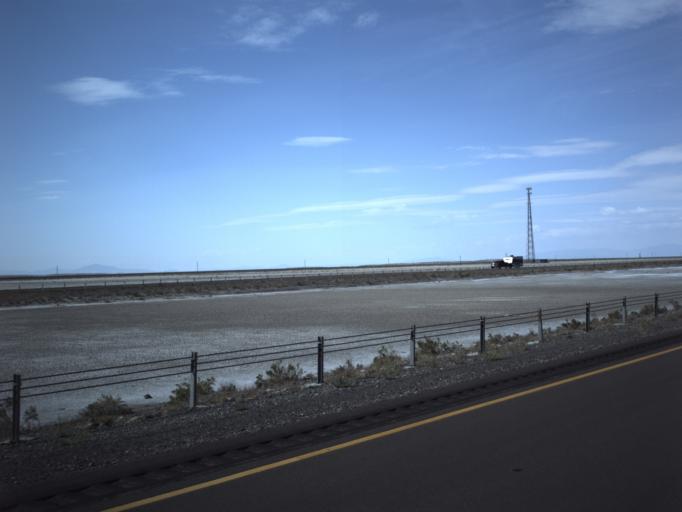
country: US
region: Utah
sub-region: Tooele County
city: Wendover
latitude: 40.7284
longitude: -113.3222
